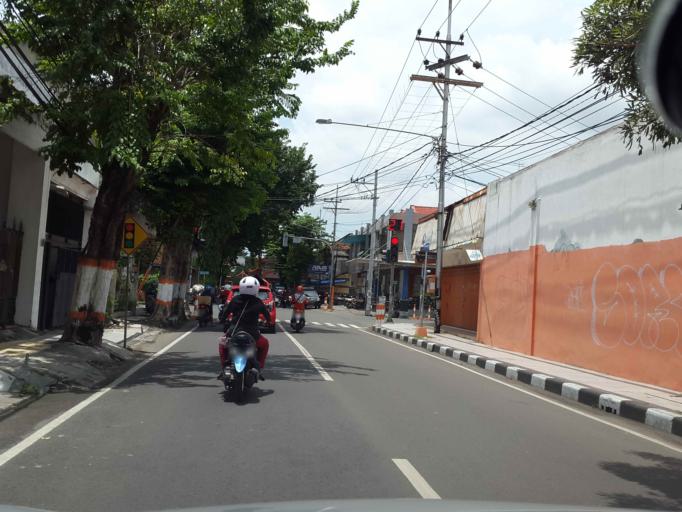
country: ID
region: East Java
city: Mojokerto
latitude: -7.4646
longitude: 112.4353
